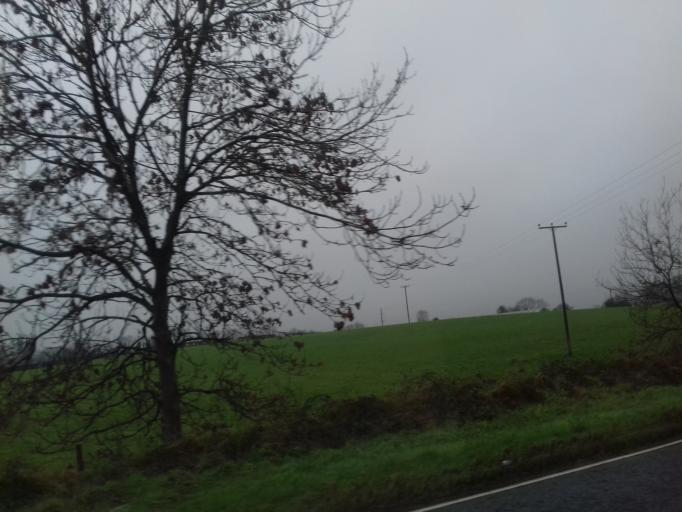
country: GB
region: Northern Ireland
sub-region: Strabane District
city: Sion Mills
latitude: 54.7565
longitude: -7.4513
